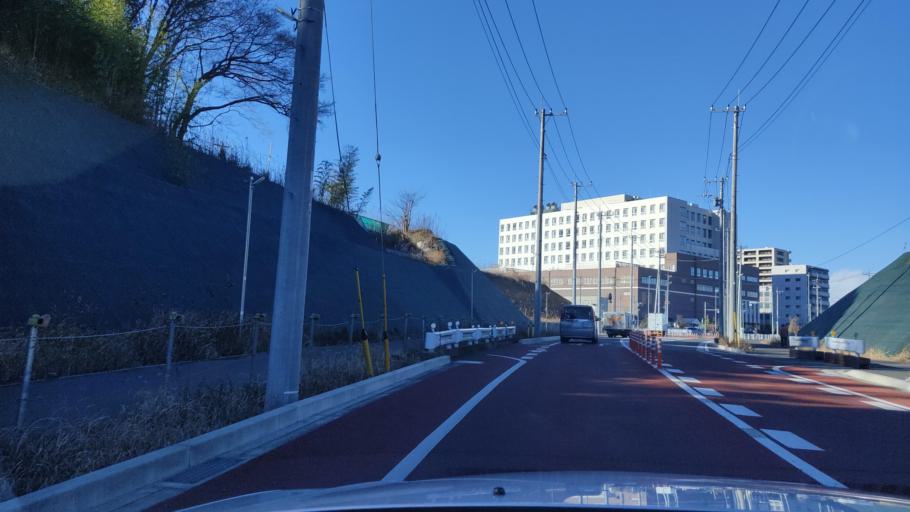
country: JP
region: Chiba
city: Nagareyama
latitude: 35.8513
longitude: 139.9174
